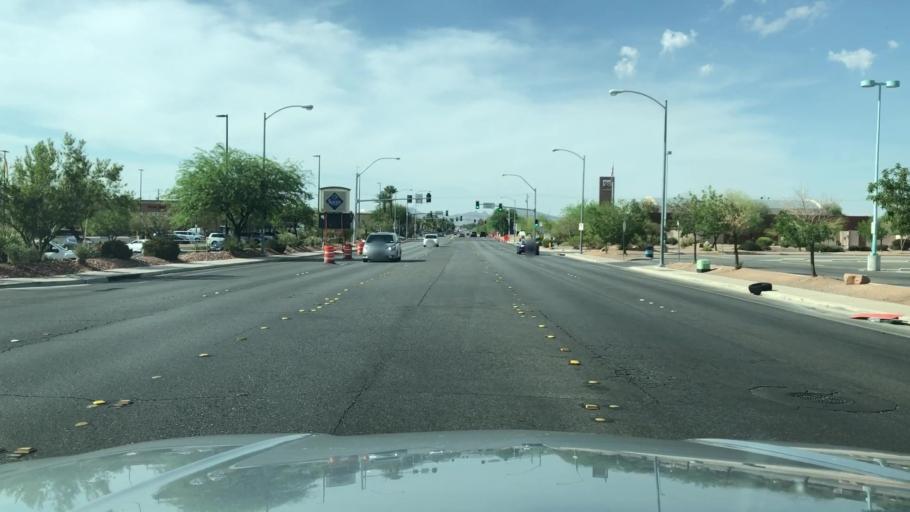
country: US
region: Nevada
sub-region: Clark County
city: Whitney
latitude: 36.0232
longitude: -115.1275
